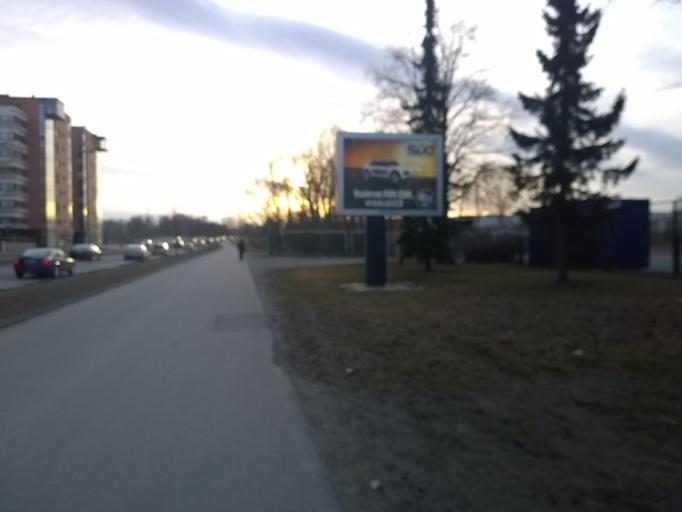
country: FI
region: Pirkanmaa
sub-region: Tampere
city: Tampere
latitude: 61.4918
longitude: 23.7631
